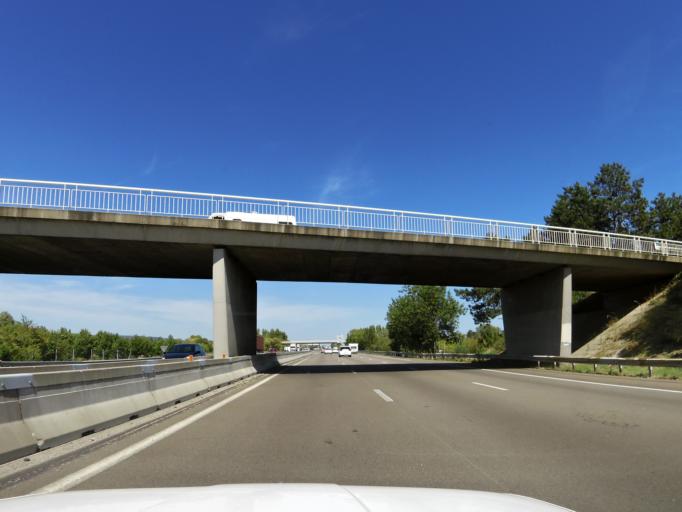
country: FR
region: Rhone-Alpes
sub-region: Departement de la Drome
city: Loriol-sur-Drome
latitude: 44.7549
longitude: 4.7927
